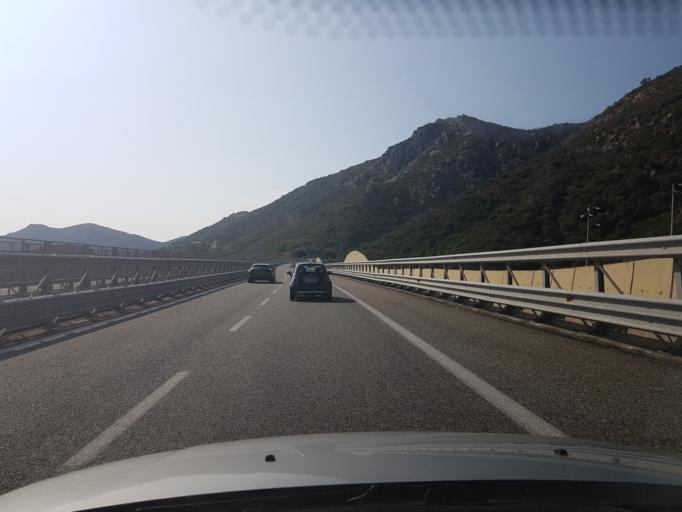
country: IT
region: Sardinia
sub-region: Provincia di Olbia-Tempio
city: San Teodoro
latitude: 40.7907
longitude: 9.6120
